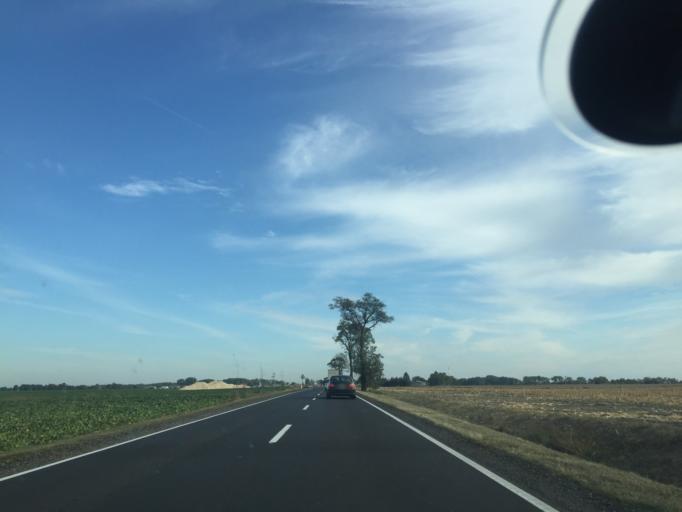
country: PL
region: Kujawsko-Pomorskie
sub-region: Powiat mogilenski
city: Mogilno
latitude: 52.6128
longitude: 17.9190
